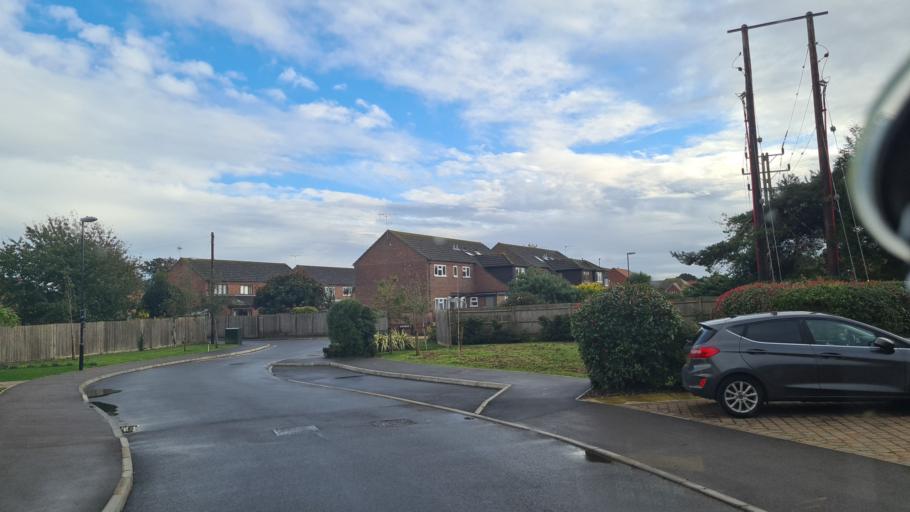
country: GB
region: England
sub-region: West Sussex
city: Walberton
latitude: 50.8194
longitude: -0.6056
